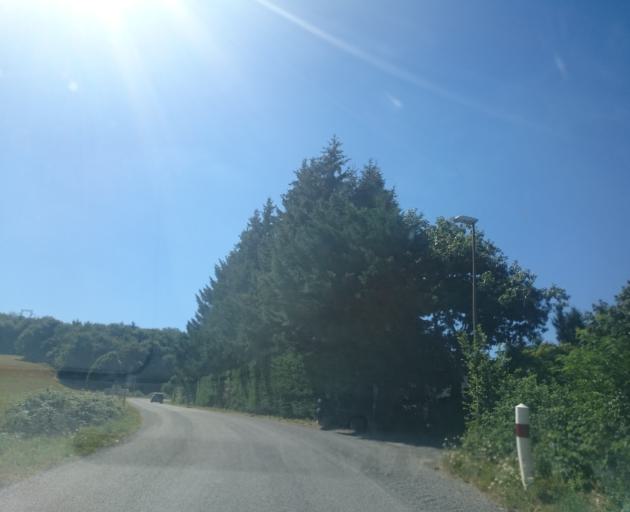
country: FR
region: Auvergne
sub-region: Departement du Cantal
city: Saint-Mamet-la-Salvetat
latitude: 44.8376
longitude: 2.3380
